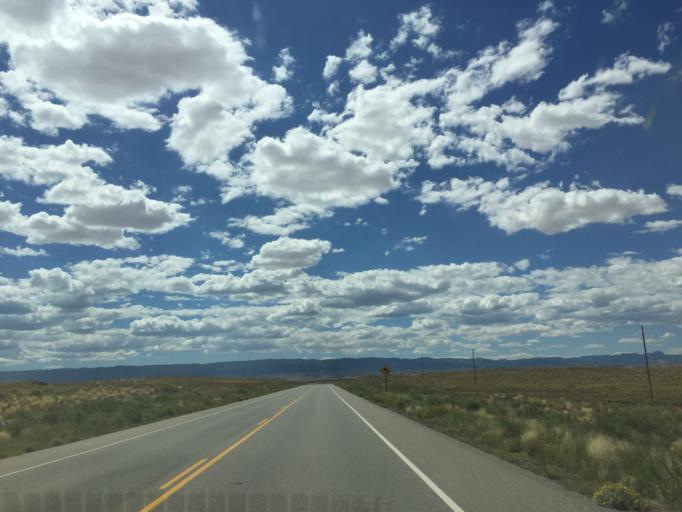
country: US
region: New Mexico
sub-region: San Juan County
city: Shiprock
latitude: 36.3434
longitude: -108.6828
